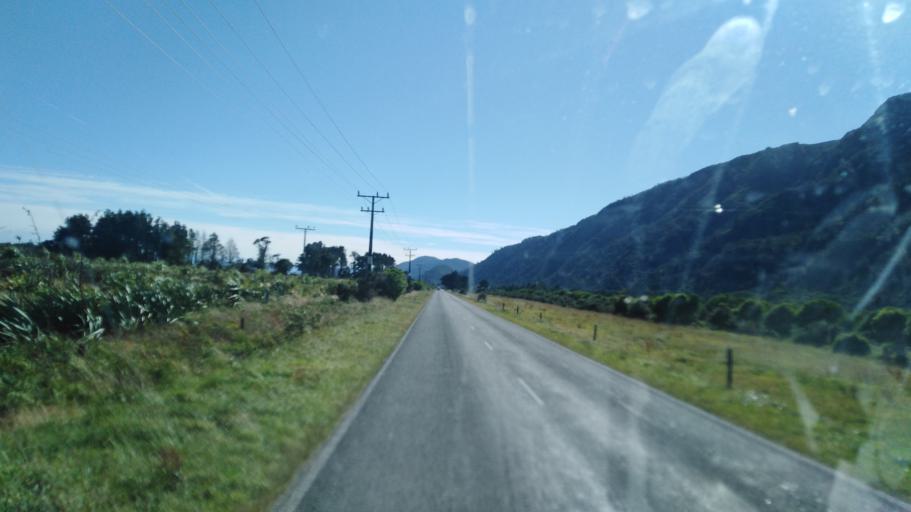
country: NZ
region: West Coast
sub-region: Buller District
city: Westport
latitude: -41.6560
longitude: 171.8233
